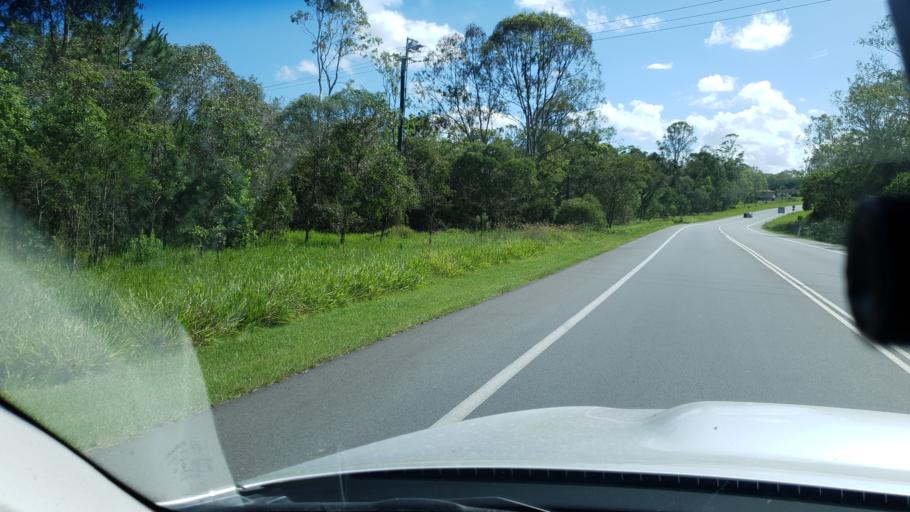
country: AU
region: Queensland
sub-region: Logan
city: Woodridge
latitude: -27.6486
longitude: 153.0859
